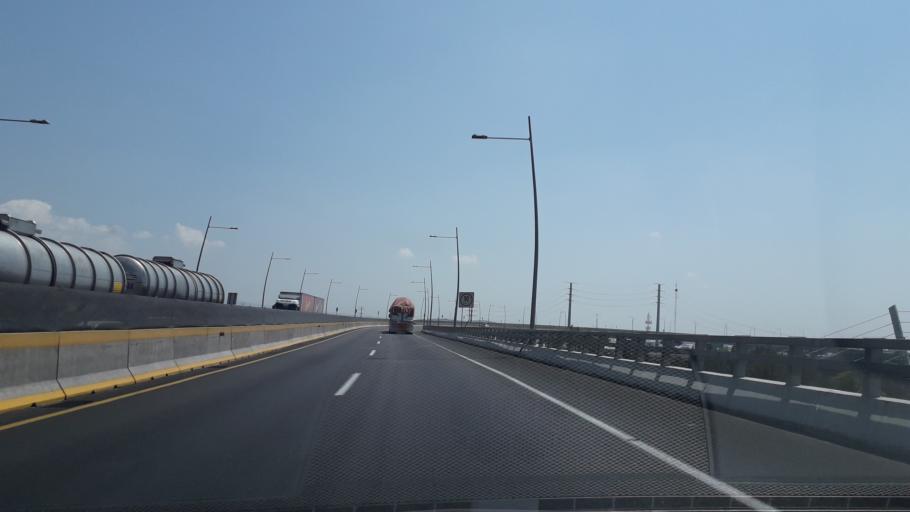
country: MX
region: Puebla
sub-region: Puebla
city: San Sebastian de Aparicio
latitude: 19.0818
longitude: -98.1688
